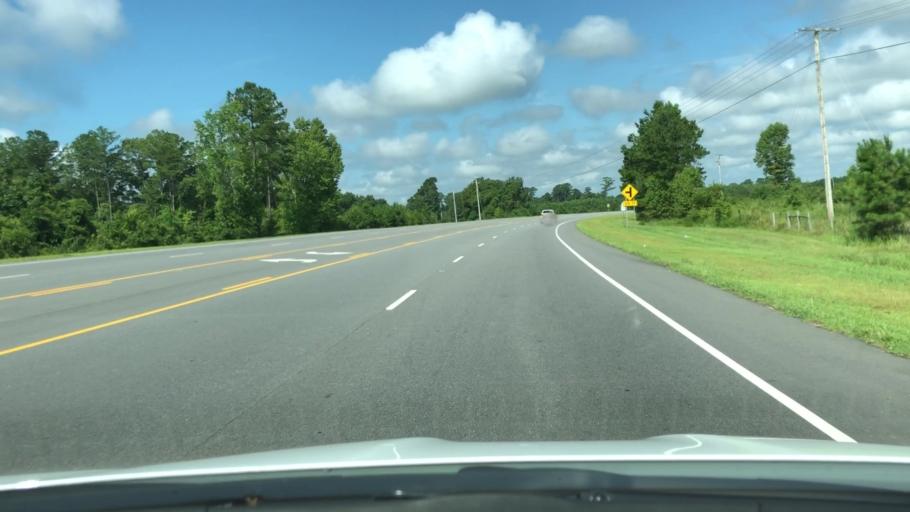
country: US
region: North Carolina
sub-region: Bertie County
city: Windsor
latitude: 36.0175
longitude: -76.8363
